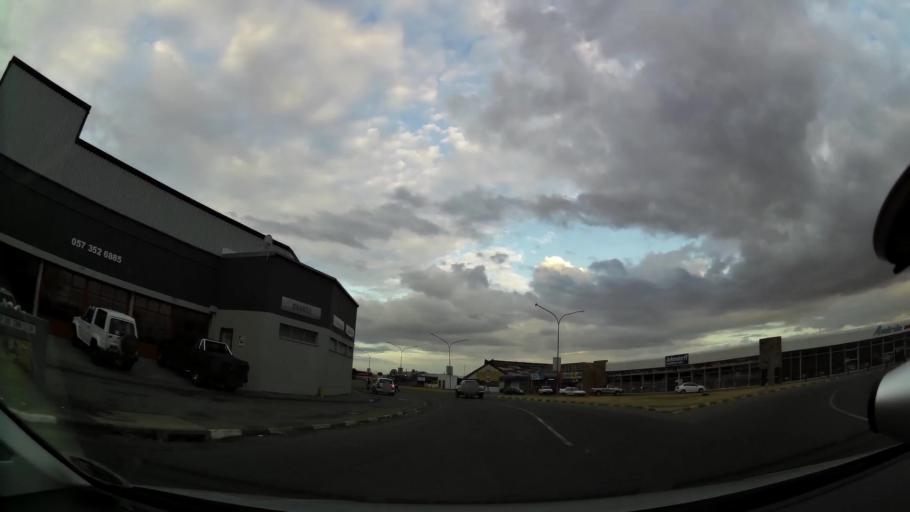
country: ZA
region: Orange Free State
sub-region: Lejweleputswa District Municipality
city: Welkom
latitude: -27.9693
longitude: 26.7487
